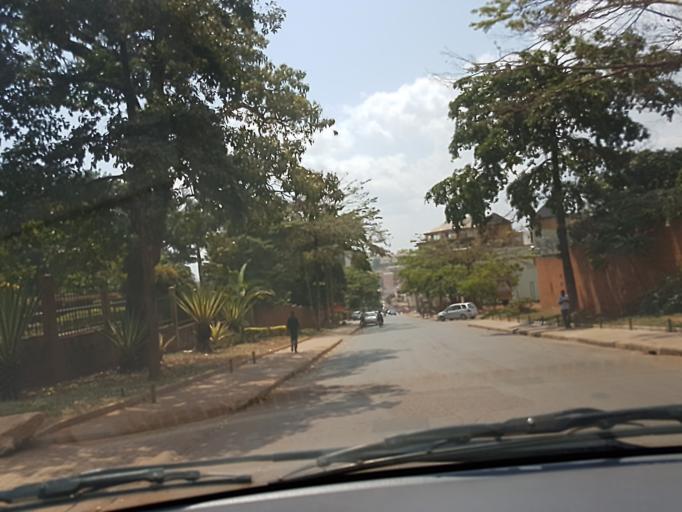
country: UG
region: Central Region
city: Kampala Central Division
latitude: 0.3195
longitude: 32.5771
